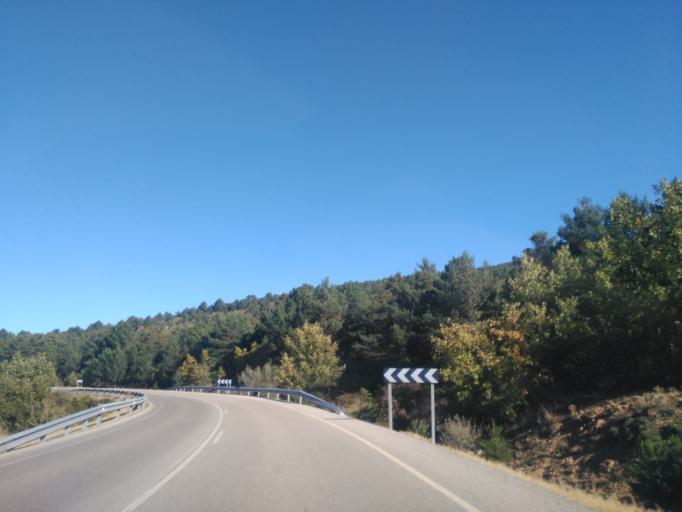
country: ES
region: Castille and Leon
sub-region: Provincia de Soria
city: Vinuesa
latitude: 41.8919
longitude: -2.7295
